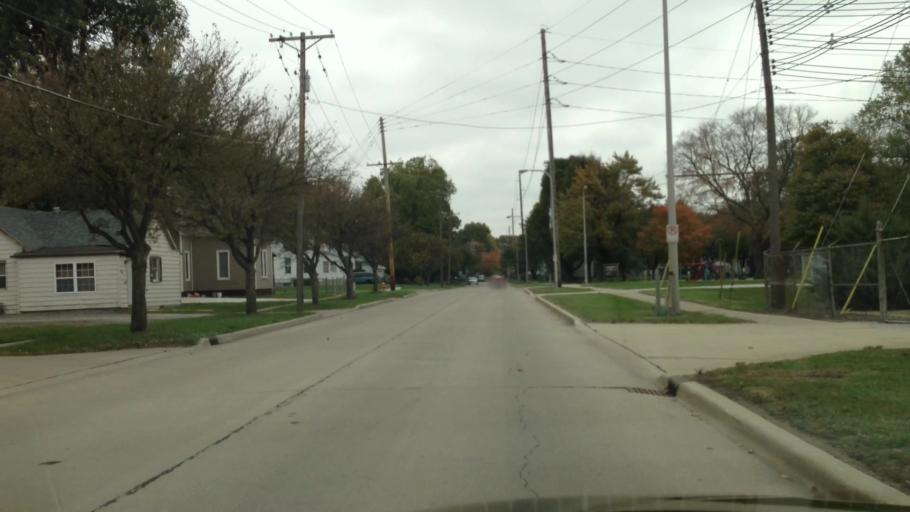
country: US
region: Illinois
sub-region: Champaign County
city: Champaign
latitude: 40.1241
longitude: -88.2411
